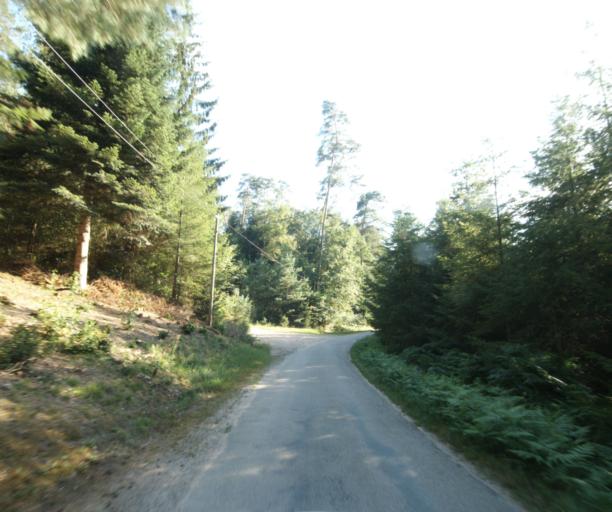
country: FR
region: Lorraine
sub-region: Departement des Vosges
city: Chantraine
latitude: 48.1423
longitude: 6.4320
